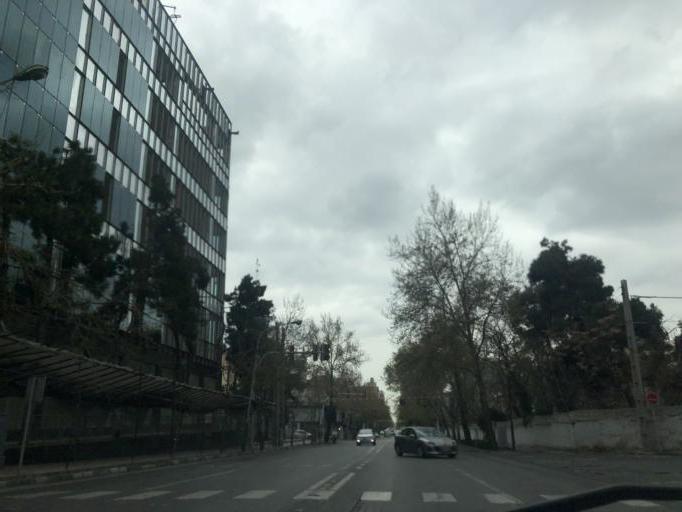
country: IR
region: Tehran
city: Tajrish
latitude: 35.7736
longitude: 51.4628
